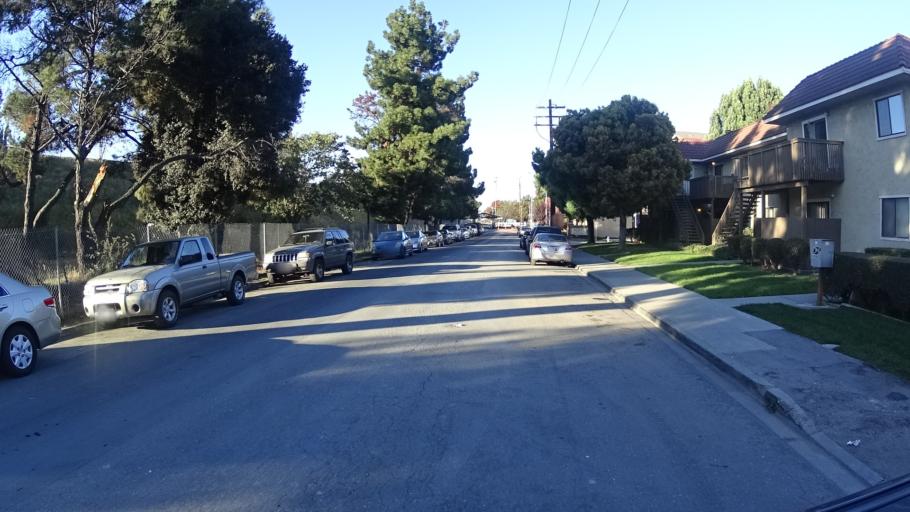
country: US
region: California
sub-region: Santa Clara County
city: Sunnyvale
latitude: 37.3690
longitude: -121.9959
